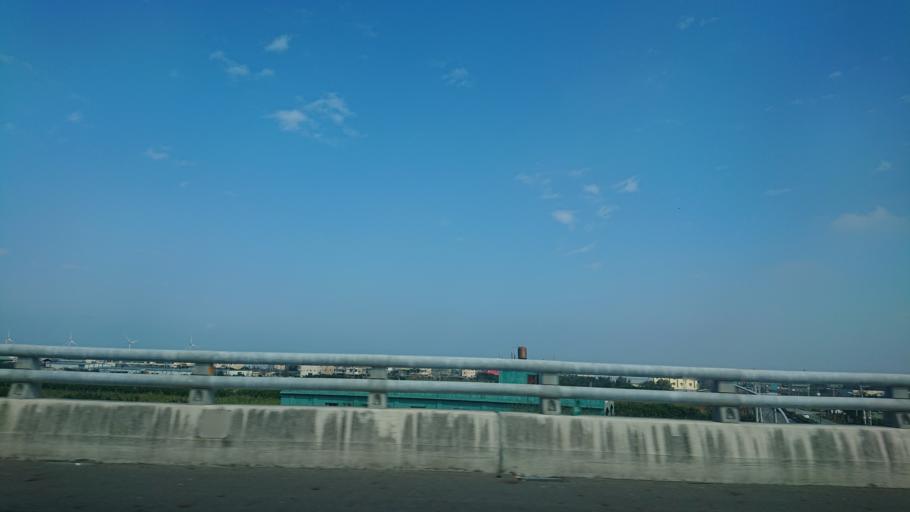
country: TW
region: Taiwan
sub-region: Changhua
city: Chang-hua
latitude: 23.9708
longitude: 120.3495
